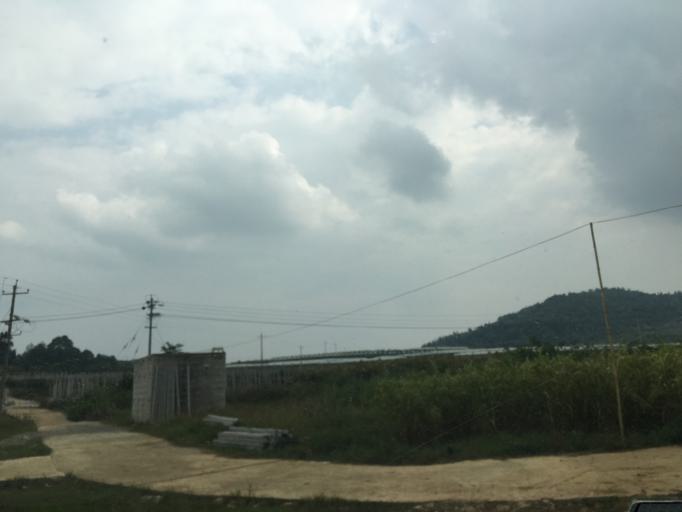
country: CN
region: Guangxi Zhuangzu Zizhiqu
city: Xinzhou
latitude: 25.4871
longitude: 105.6510
